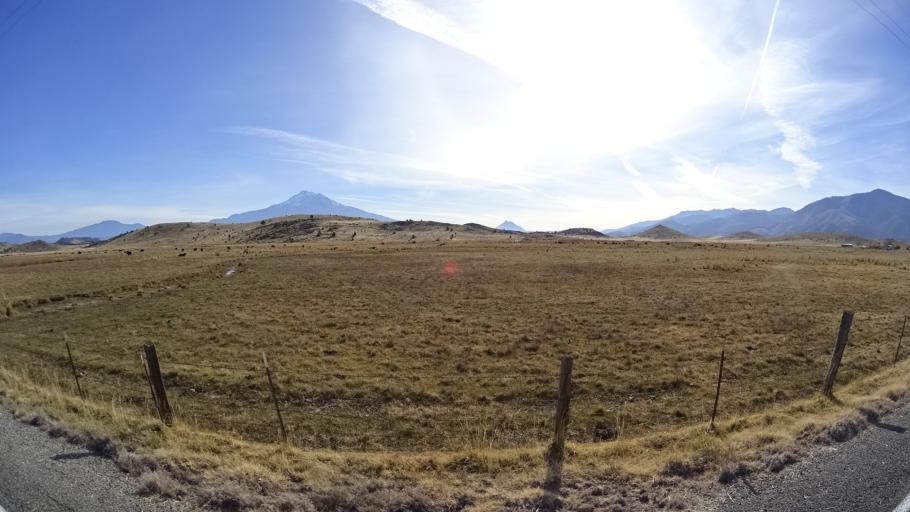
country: US
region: California
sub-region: Siskiyou County
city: Weed
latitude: 41.5352
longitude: -122.5082
